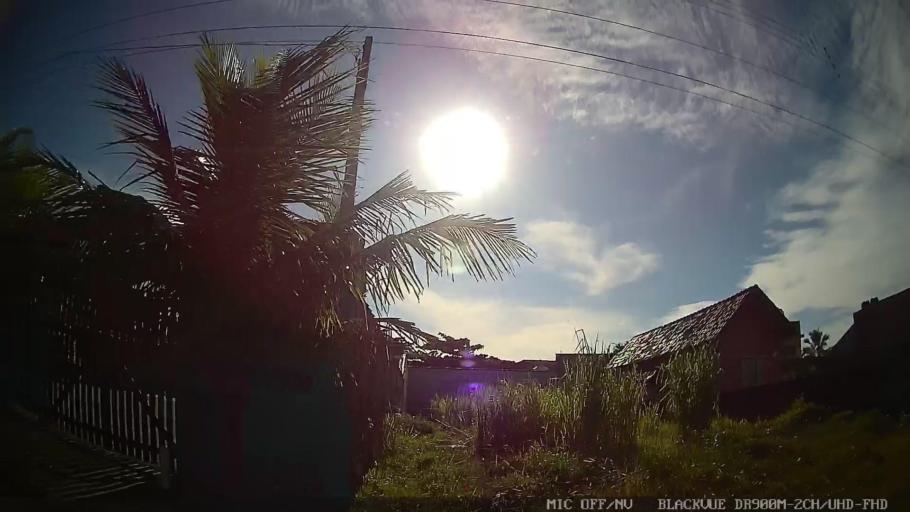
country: BR
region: Sao Paulo
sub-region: Iguape
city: Iguape
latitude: -24.7638
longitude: -47.5774
